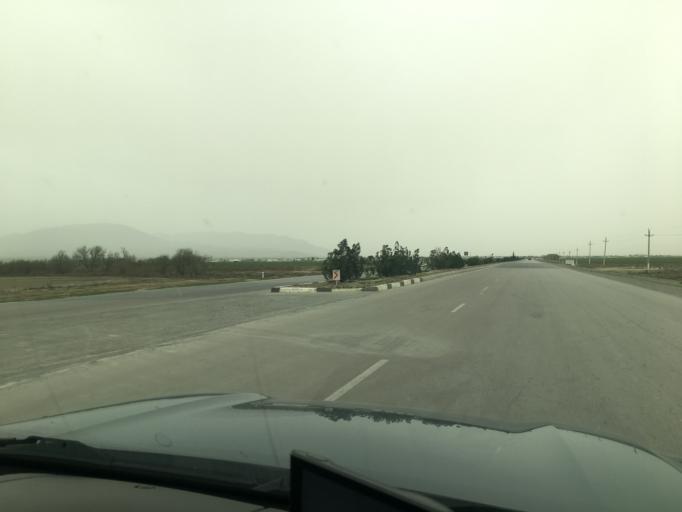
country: TM
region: Ahal
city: Baharly
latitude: 38.3845
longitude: 57.4959
